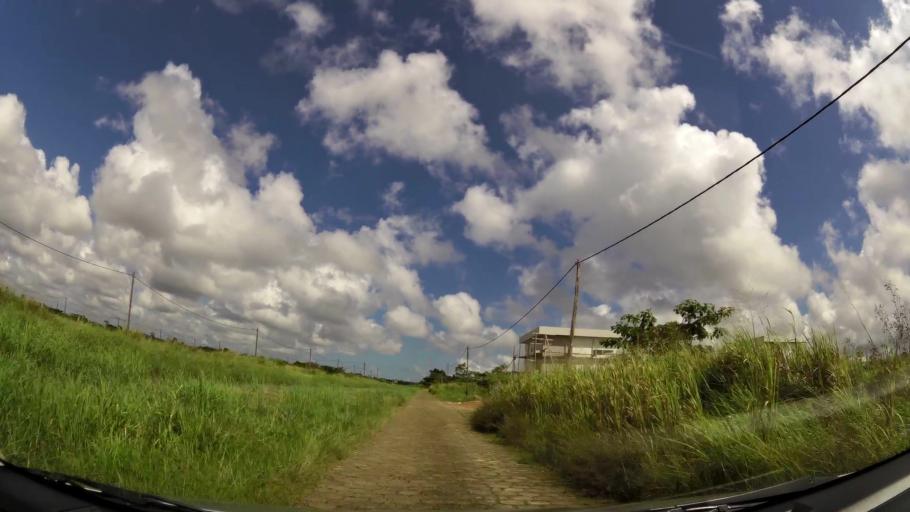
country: SR
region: Paramaribo
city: Paramaribo
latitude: 5.8693
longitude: -55.1252
